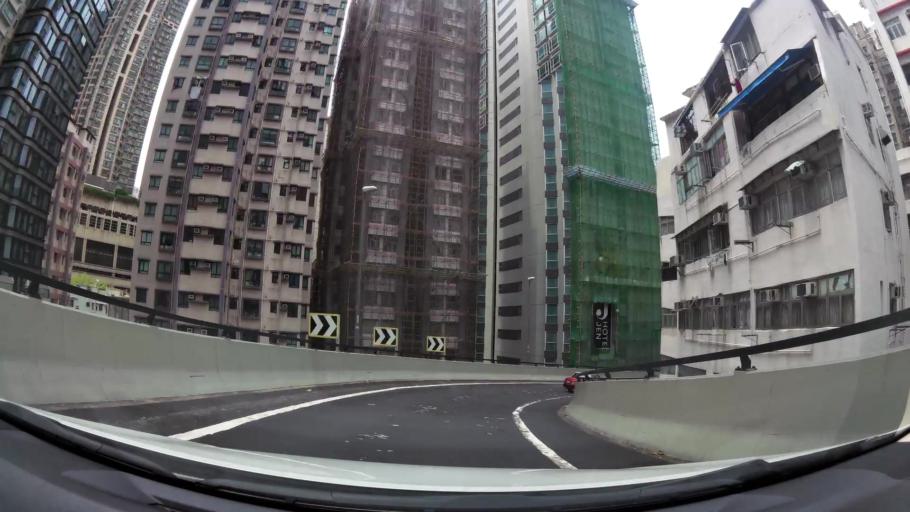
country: HK
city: Hong Kong
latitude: 22.2856
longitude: 114.1354
